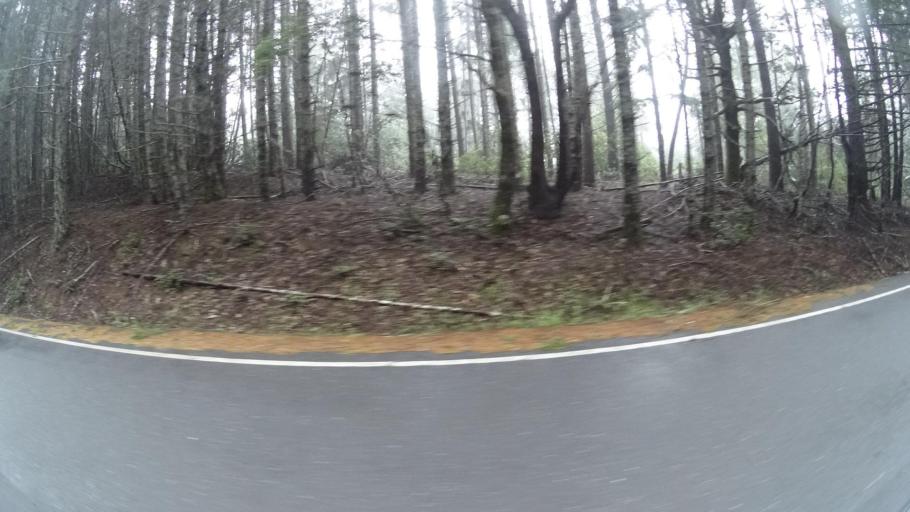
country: US
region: California
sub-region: Humboldt County
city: Westhaven-Moonstone
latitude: 41.2129
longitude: -123.9566
